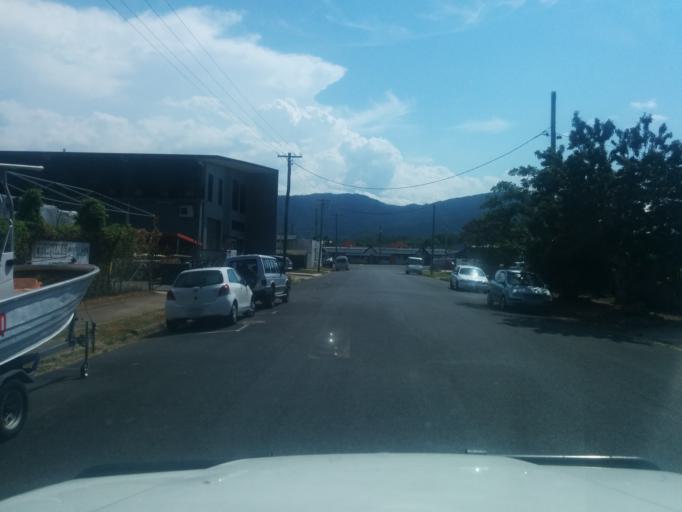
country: AU
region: Queensland
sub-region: Cairns
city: Woree
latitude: -16.9386
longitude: 145.7529
